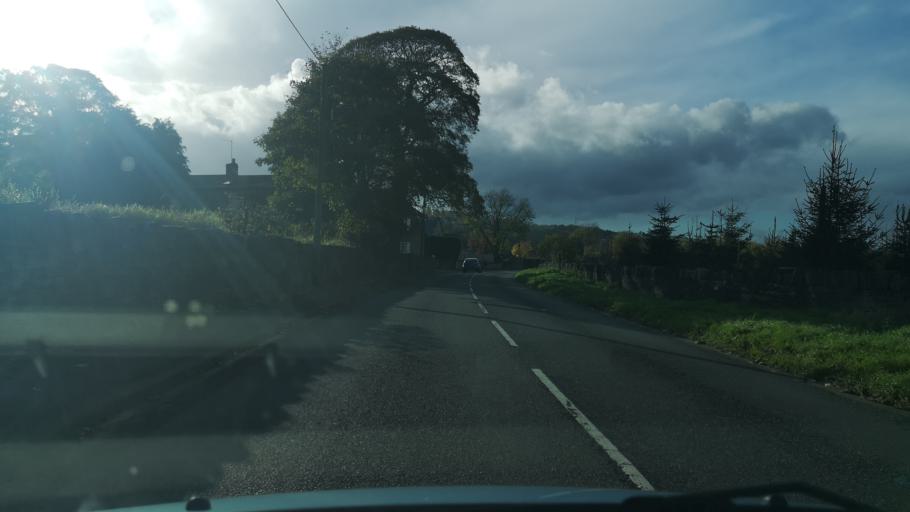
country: GB
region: England
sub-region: Kirklees
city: Mirfield
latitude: 53.6686
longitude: -1.6824
